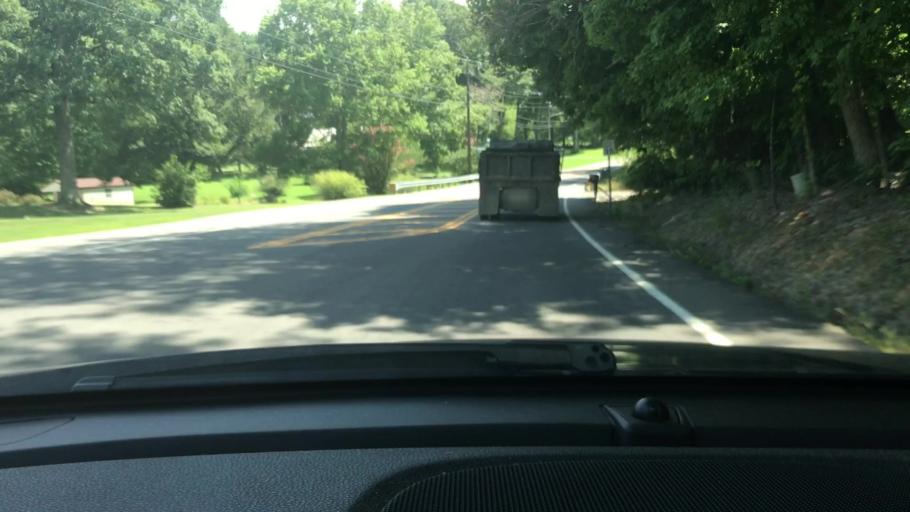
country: US
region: Tennessee
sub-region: Sumner County
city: White House
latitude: 36.4481
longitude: -86.6447
